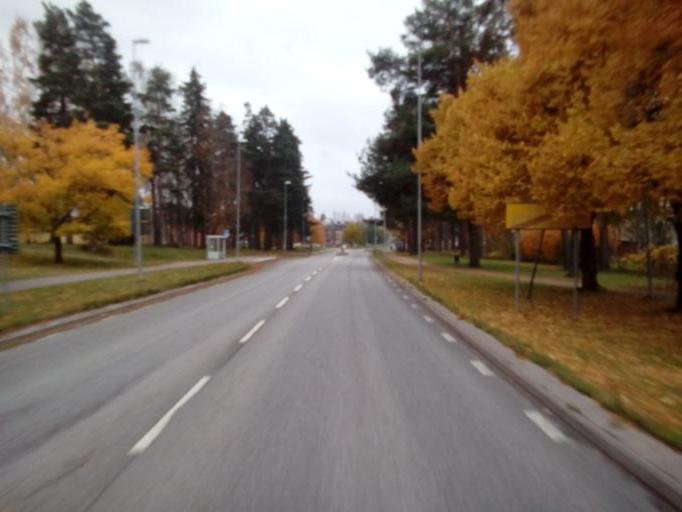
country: SE
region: OErebro
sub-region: Degerfors Kommun
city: Degerfors
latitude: 59.2444
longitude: 14.4356
